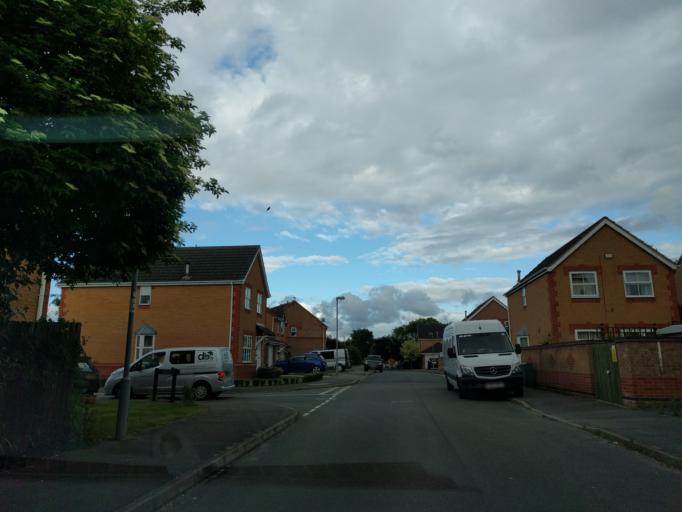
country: GB
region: England
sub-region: Nottinghamshire
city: Newark on Trent
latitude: 53.0491
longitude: -0.7832
